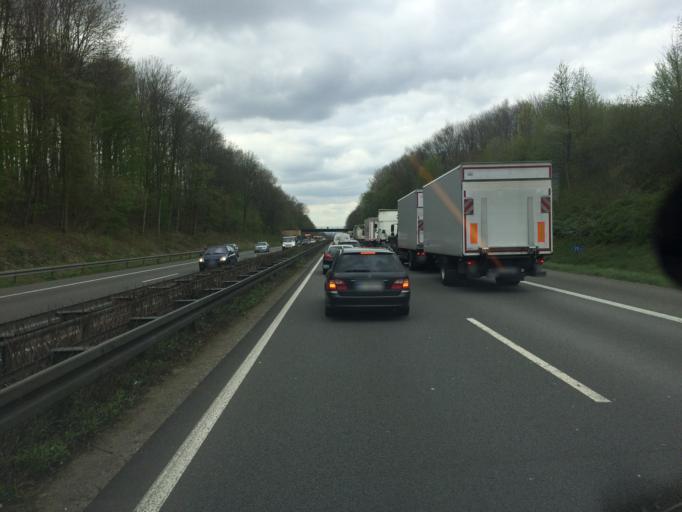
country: DE
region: North Rhine-Westphalia
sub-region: Regierungsbezirk Arnsberg
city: Herne
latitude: 51.5075
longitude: 7.2435
